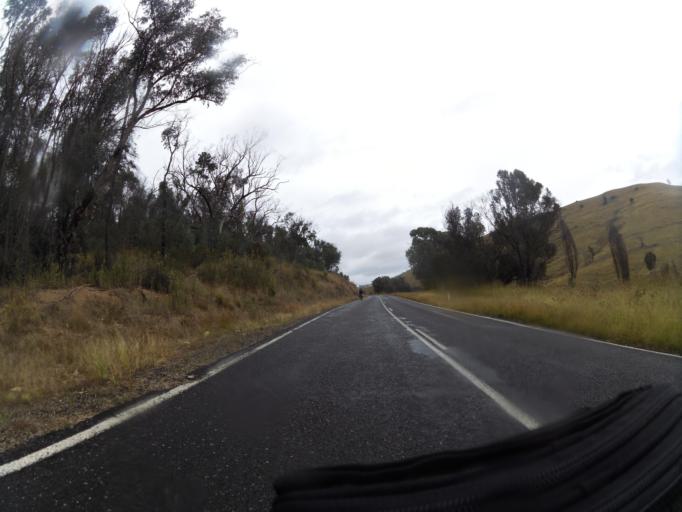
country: AU
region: New South Wales
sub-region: Greater Hume Shire
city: Holbrook
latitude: -36.2241
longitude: 147.7267
